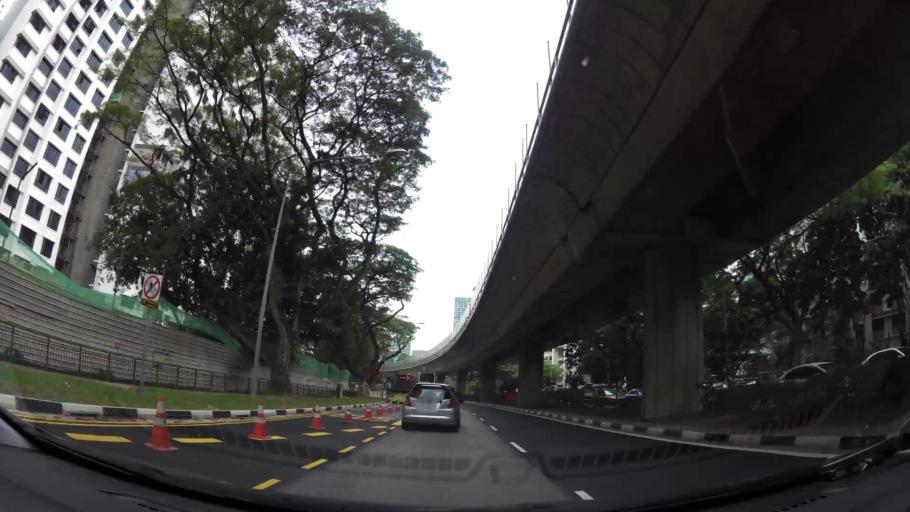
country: SG
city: Singapore
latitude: 1.3085
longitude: 103.7837
